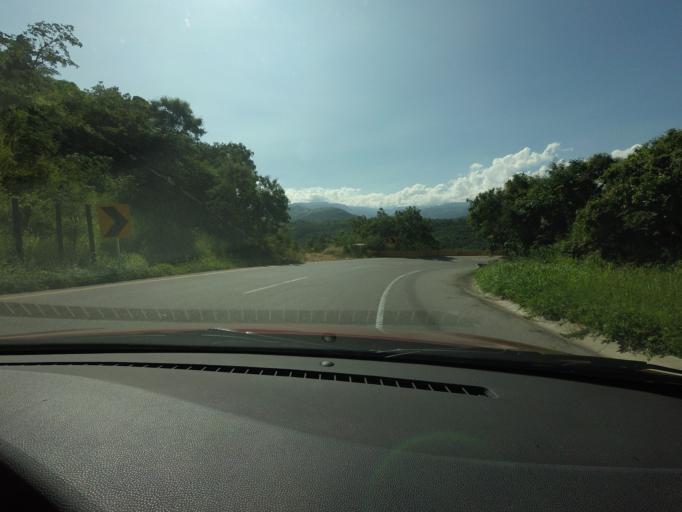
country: CO
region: Cundinamarca
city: Pandi
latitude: 4.2552
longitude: -74.5234
